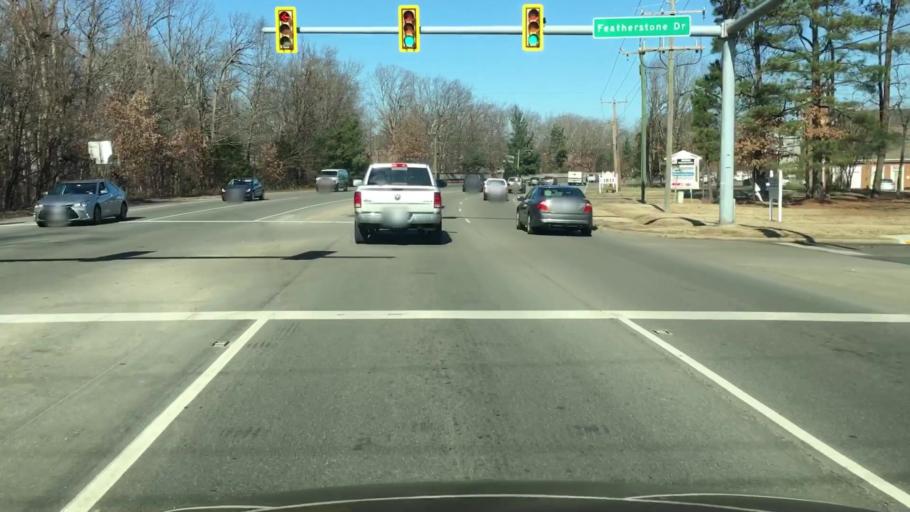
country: US
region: Virginia
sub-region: Chesterfield County
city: Bon Air
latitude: 37.5176
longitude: -77.6159
